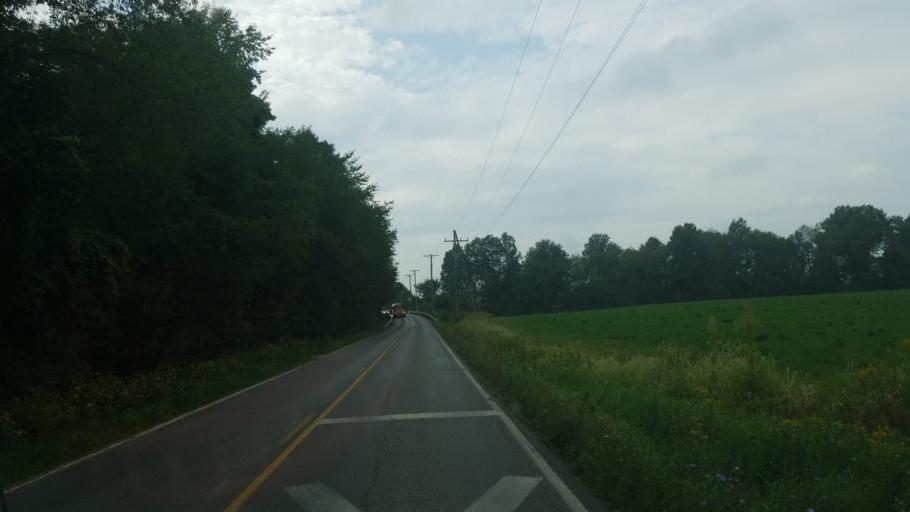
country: US
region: Ohio
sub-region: Wayne County
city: Creston
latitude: 40.9606
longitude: -81.8771
